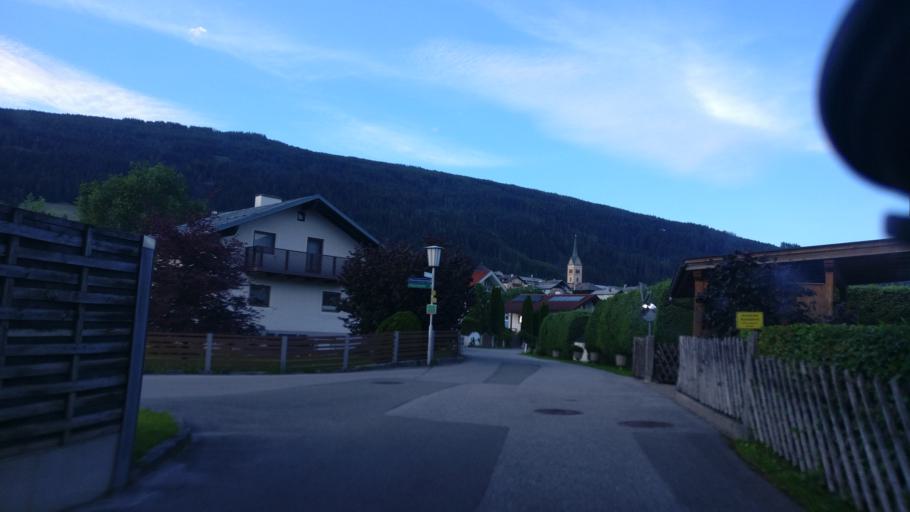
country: AT
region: Salzburg
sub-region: Politischer Bezirk Sankt Johann im Pongau
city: Radstadt
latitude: 47.3813
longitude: 13.4593
